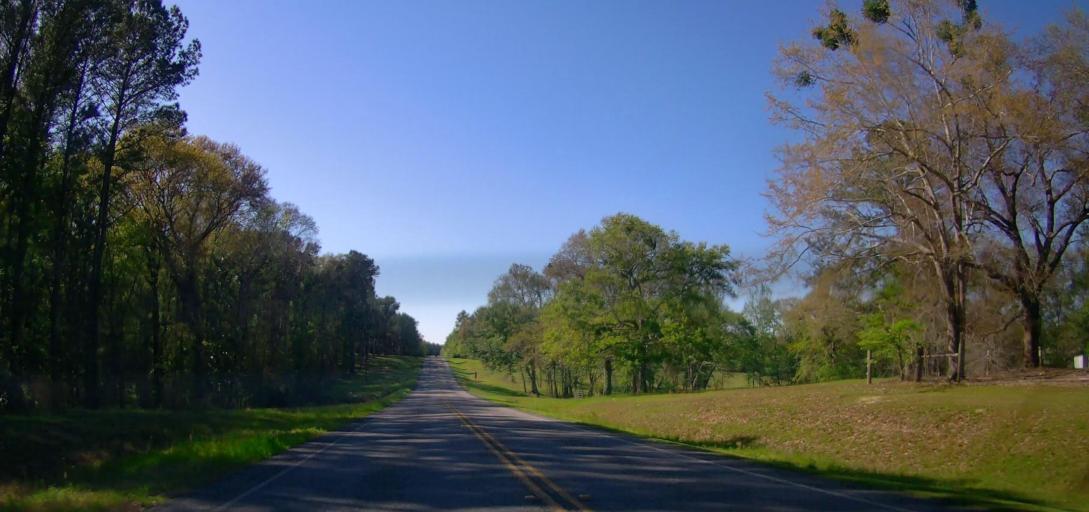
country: US
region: Georgia
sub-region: Wilcox County
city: Rochelle
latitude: 32.0058
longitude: -83.4860
